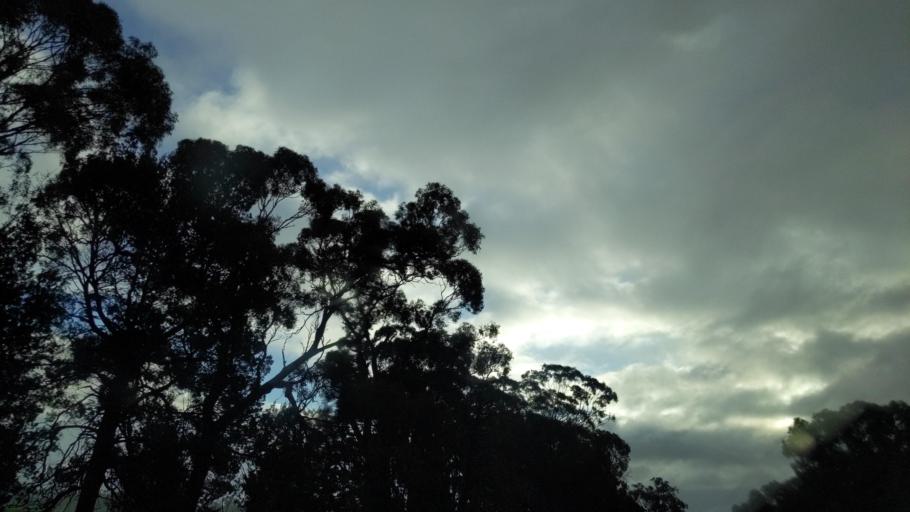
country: AU
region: New South Wales
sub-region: Coolamon
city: Coolamon
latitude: -34.8662
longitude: 147.2463
